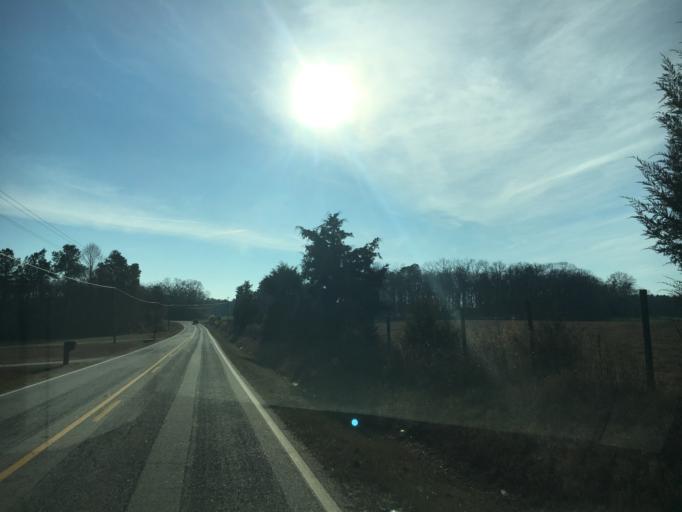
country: US
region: Georgia
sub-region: Hart County
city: Reed Creek
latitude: 34.4318
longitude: -82.9374
